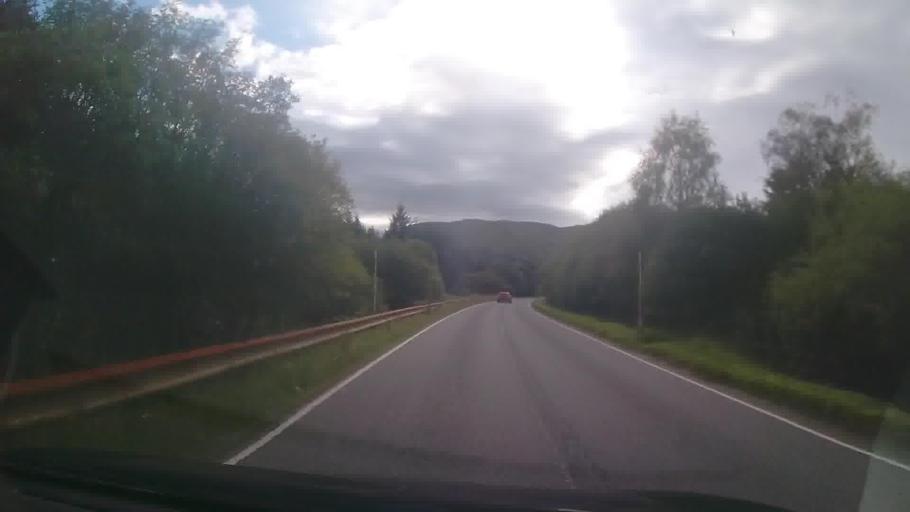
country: GB
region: Scotland
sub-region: Argyll and Bute
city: Garelochhead
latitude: 56.3215
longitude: -5.0802
